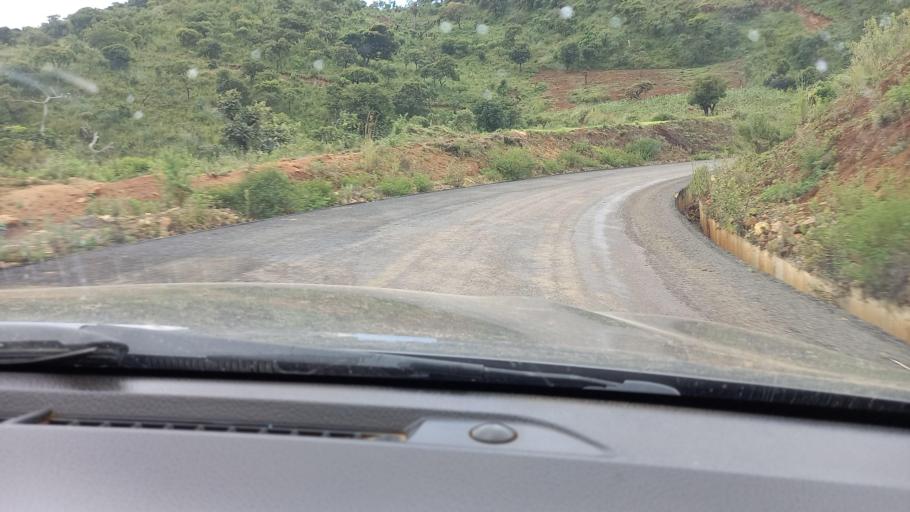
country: ET
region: Southern Nations, Nationalities, and People's Region
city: Mizan Teferi
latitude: 6.2027
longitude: 35.6519
